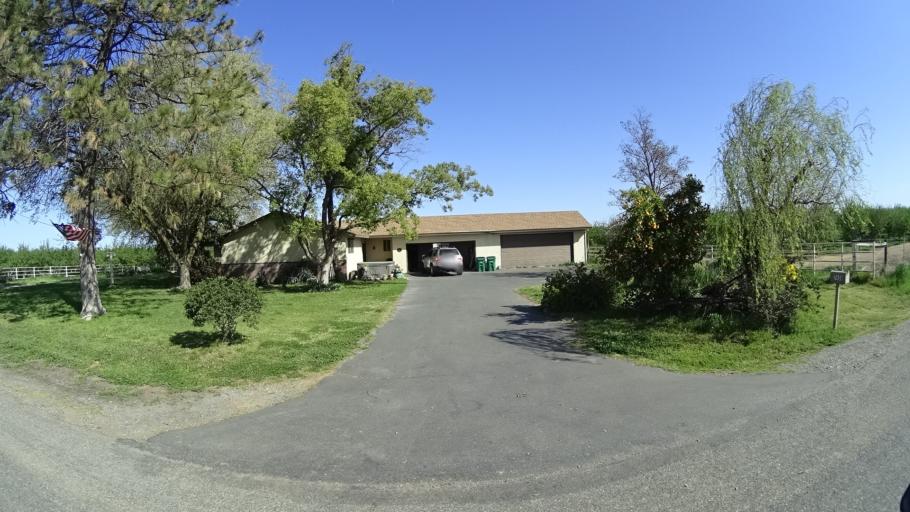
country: US
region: California
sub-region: Glenn County
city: Hamilton City
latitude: 39.7824
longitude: -122.0710
